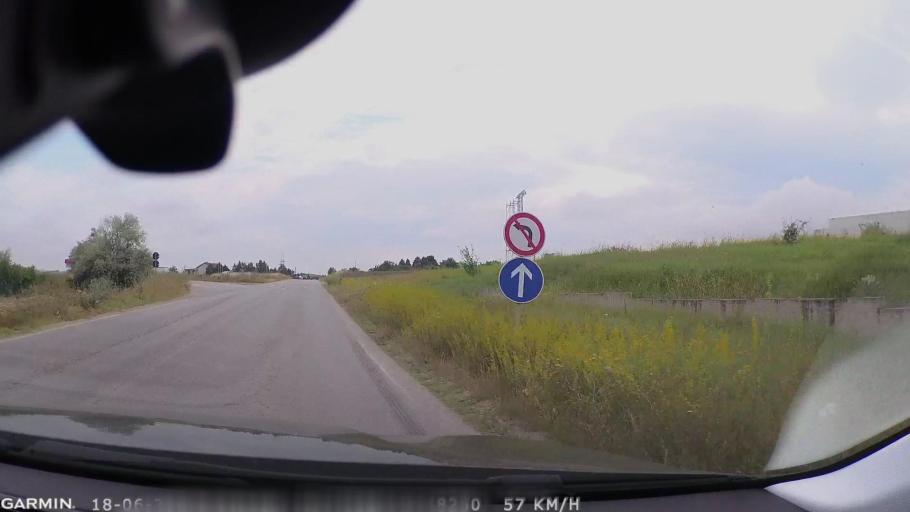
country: MK
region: Stip
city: Shtip
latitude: 41.7736
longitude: 22.1825
